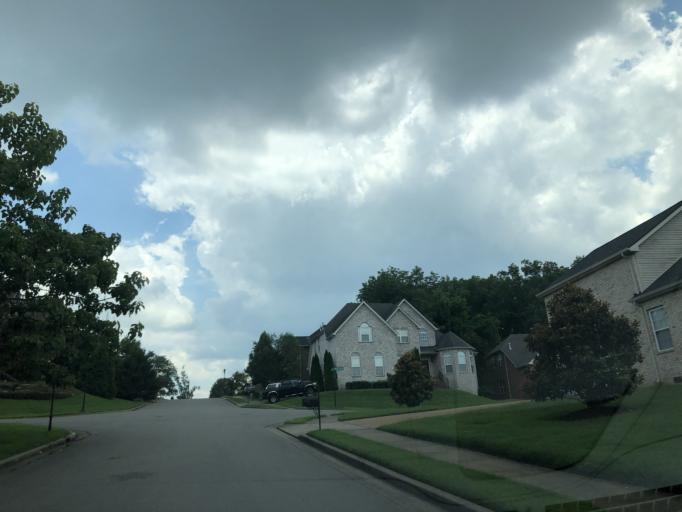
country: US
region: Tennessee
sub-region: Williamson County
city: Brentwood Estates
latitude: 36.0186
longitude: -86.7152
